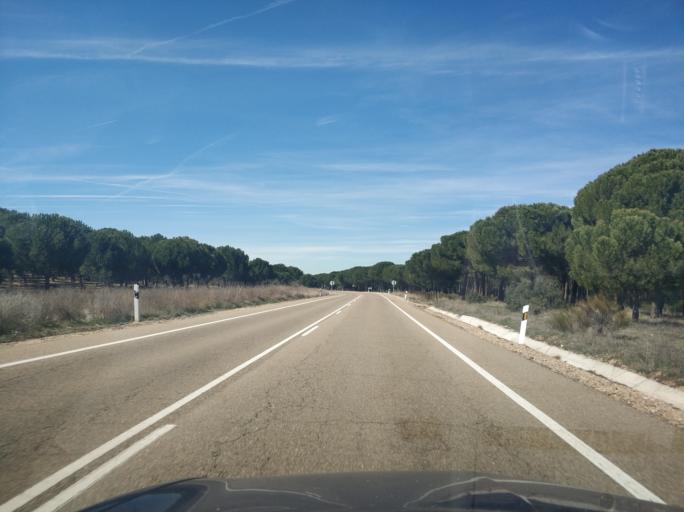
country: ES
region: Castille and Leon
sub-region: Provincia de Valladolid
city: Viana de Cega
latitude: 41.5385
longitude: -4.7683
